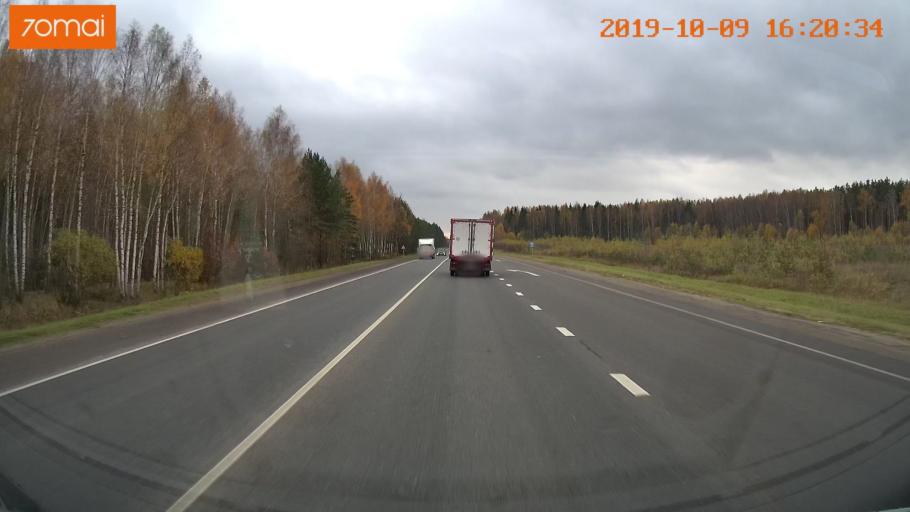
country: RU
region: Kostroma
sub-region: Kostromskoy Rayon
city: Kostroma
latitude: 57.7049
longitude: 40.8918
